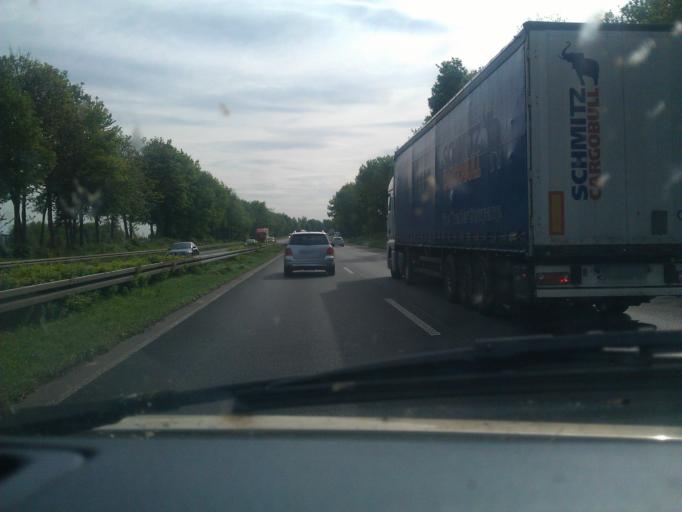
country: DE
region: North Rhine-Westphalia
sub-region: Regierungsbezirk Dusseldorf
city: Grevenbroich
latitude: 51.1135
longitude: 6.5847
